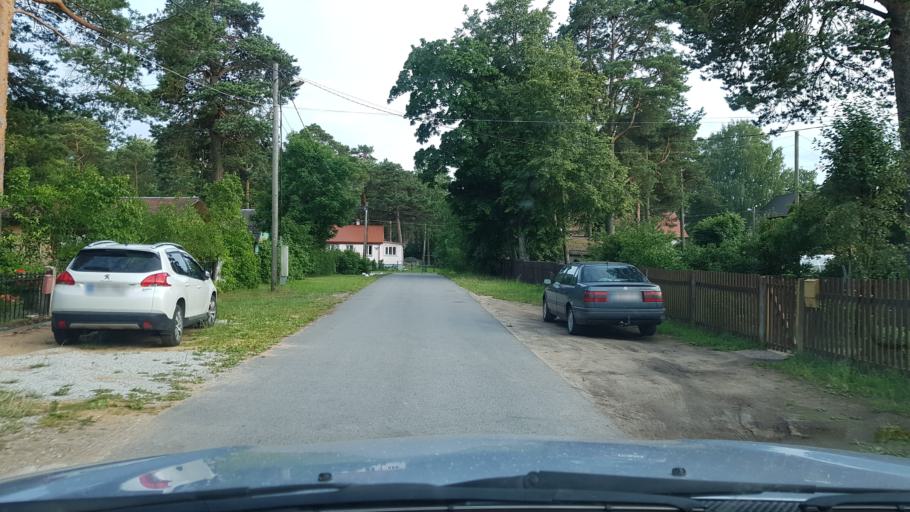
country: EE
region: Ida-Virumaa
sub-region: Narva-Joesuu linn
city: Narva-Joesuu
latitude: 59.4571
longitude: 28.0517
